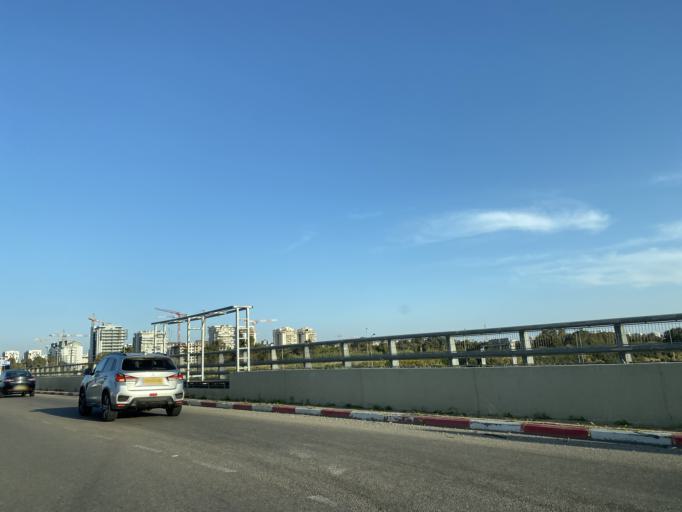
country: IL
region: Tel Aviv
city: Kefar Shemaryahu
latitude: 32.1790
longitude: 34.8244
